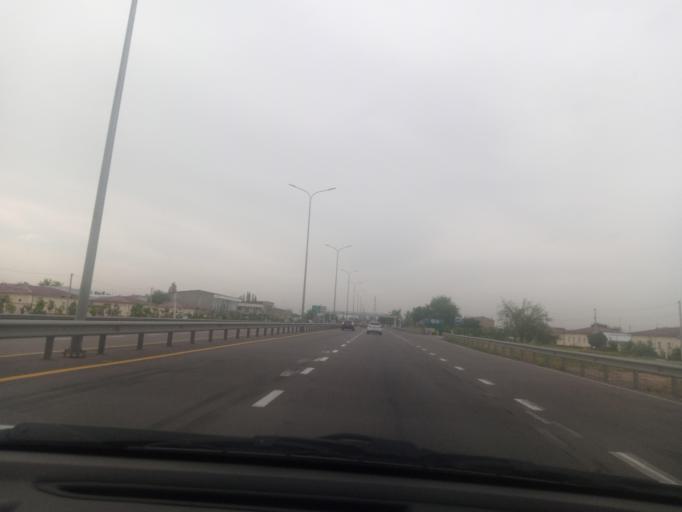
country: UZ
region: Toshkent
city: Tuytepa
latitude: 41.1329
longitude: 69.4355
